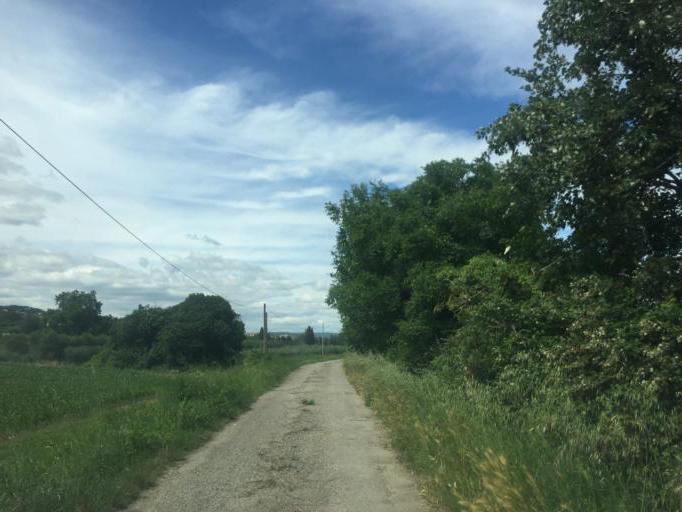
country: FR
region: Rhone-Alpes
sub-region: Departement de l'Ardeche
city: Bourg-Saint-Andeol
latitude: 44.3558
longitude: 4.6457
